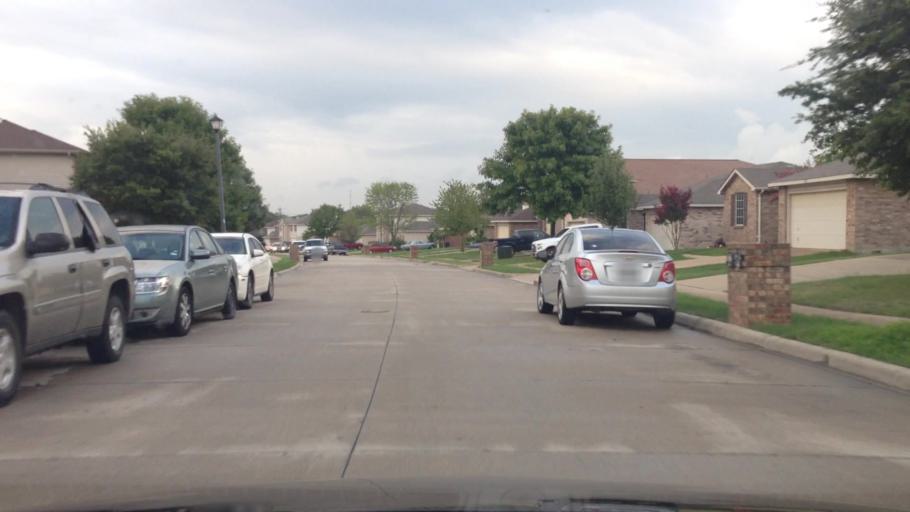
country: US
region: Texas
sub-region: Tarrant County
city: Crowley
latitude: 32.5642
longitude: -97.3406
